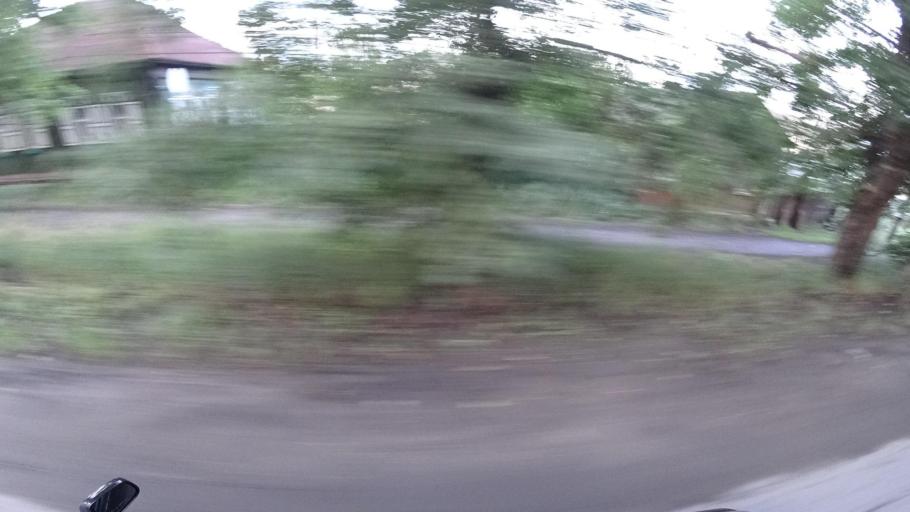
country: RU
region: Sverdlovsk
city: Kamyshlov
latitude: 56.8578
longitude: 62.7077
